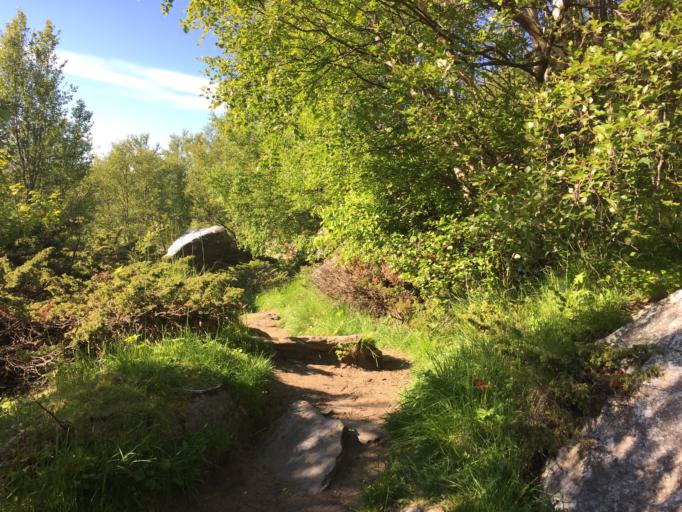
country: NO
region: Nordland
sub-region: Bodo
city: Loding
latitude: 67.4169
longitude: 14.6325
